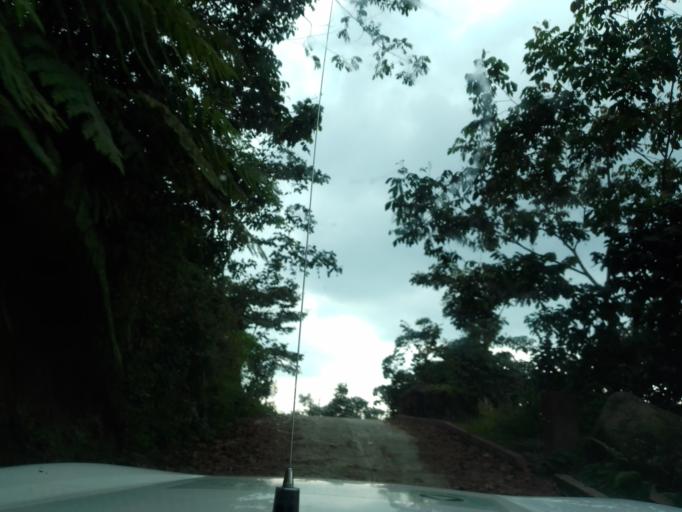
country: MX
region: Chiapas
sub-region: Union Juarez
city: Santo Domingo
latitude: 15.0678
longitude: -92.1163
